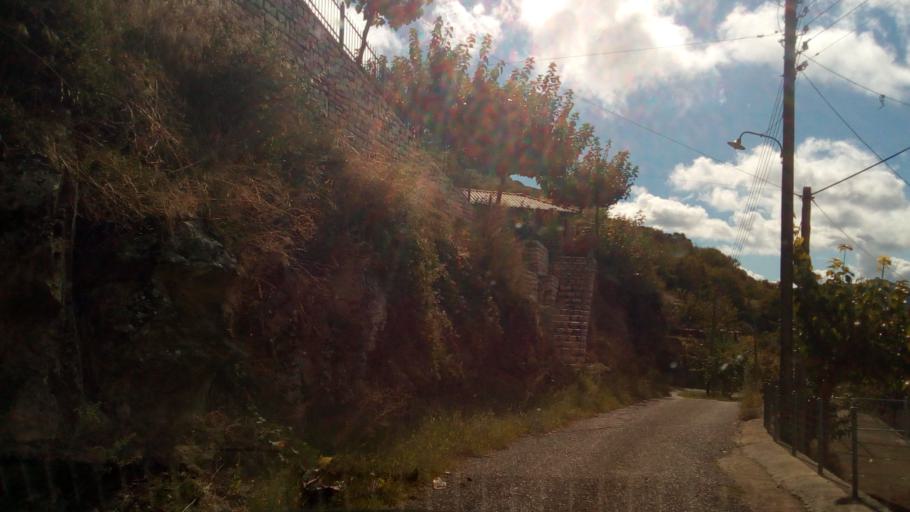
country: GR
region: West Greece
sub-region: Nomos Aitolias kai Akarnanias
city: Nafpaktos
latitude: 38.4926
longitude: 21.8523
